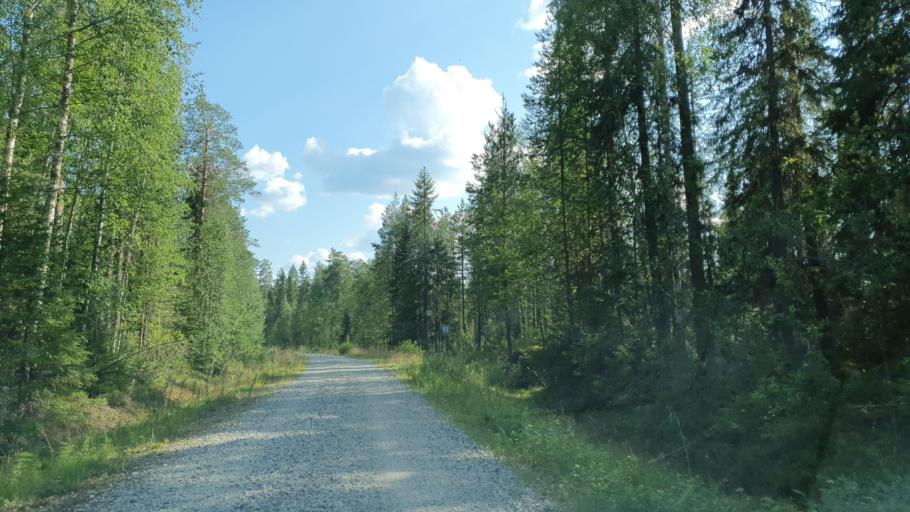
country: FI
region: Kainuu
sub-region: Kehys-Kainuu
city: Kuhmo
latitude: 63.9581
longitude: 29.5532
